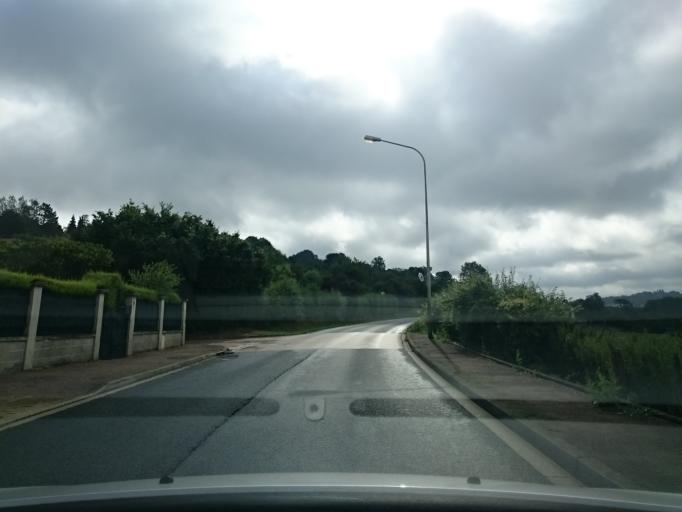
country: FR
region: Lower Normandy
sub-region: Departement du Calvados
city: Beuvillers
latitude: 49.1300
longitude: 0.2660
